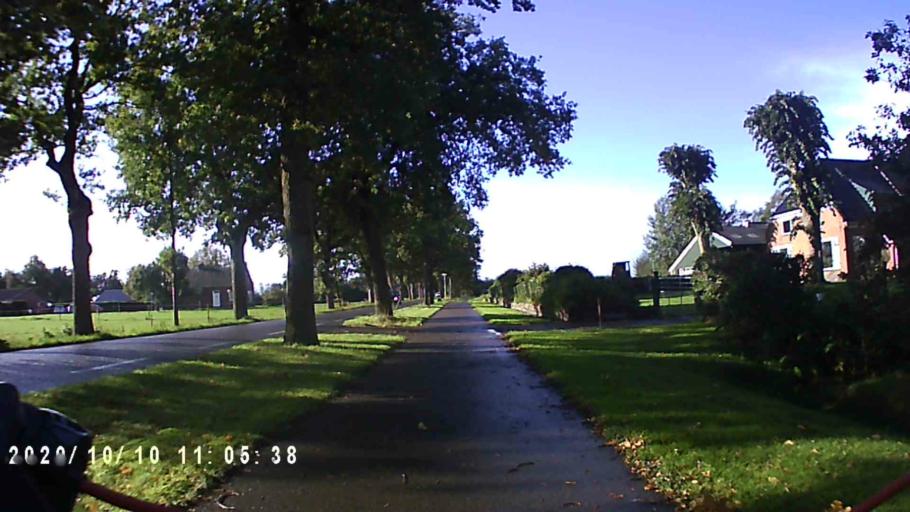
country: NL
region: Friesland
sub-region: Gemeente Achtkarspelen
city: Surhuisterveen
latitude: 53.1283
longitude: 6.2204
